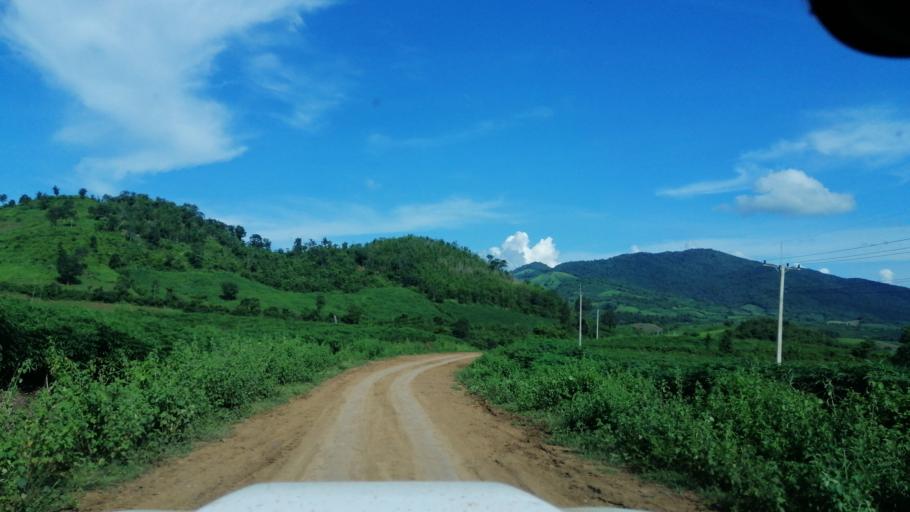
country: TH
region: Uttaradit
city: Ban Khok
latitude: 17.9052
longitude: 101.2074
